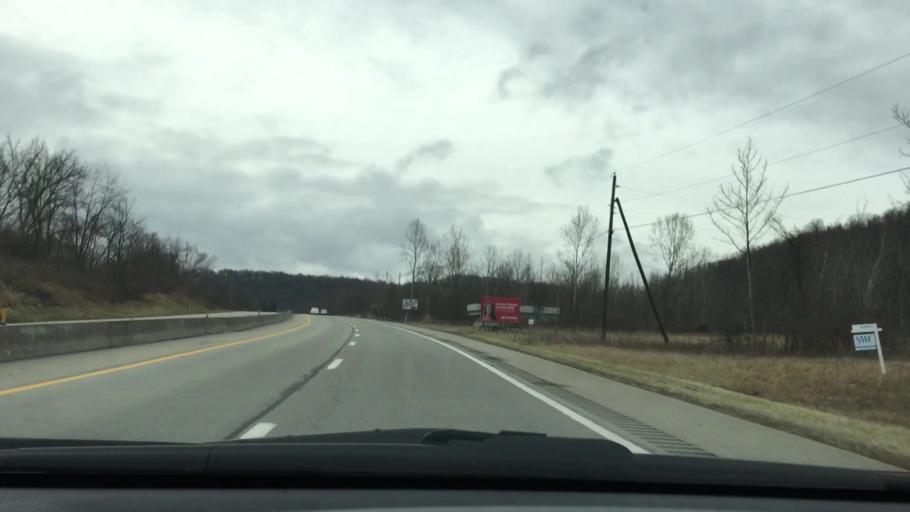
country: US
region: Pennsylvania
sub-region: Fayette County
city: Oliver
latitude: 39.9870
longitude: -79.7659
